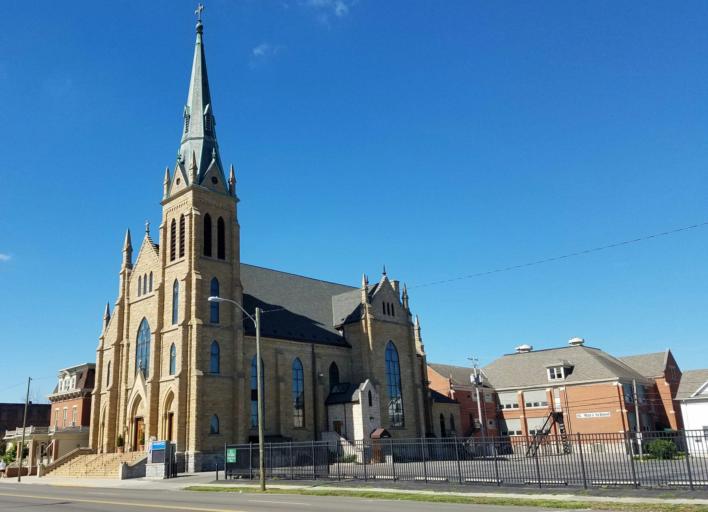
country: US
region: Ohio
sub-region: Marion County
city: Marion
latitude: 40.5920
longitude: -83.1290
